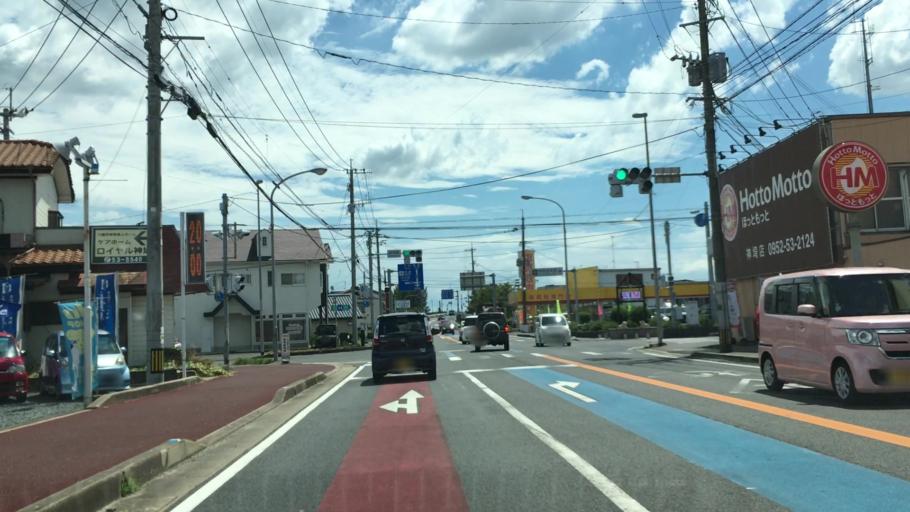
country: JP
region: Saga Prefecture
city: Kanzakimachi-kanzaki
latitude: 33.3077
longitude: 130.3702
